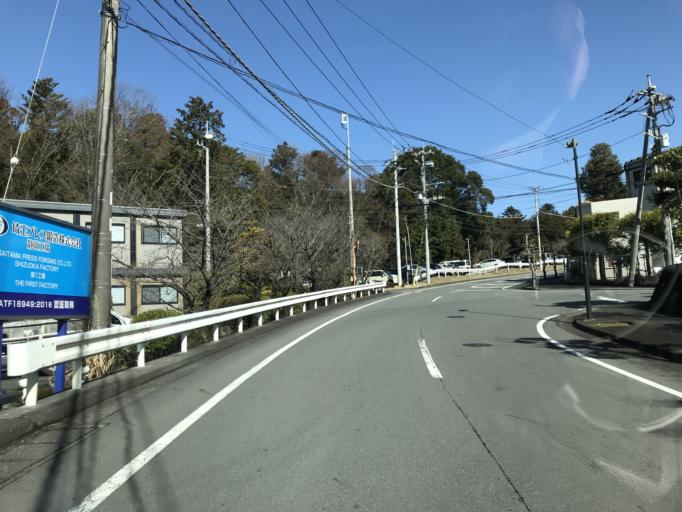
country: JP
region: Shizuoka
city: Fujinomiya
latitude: 35.2678
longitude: 138.6439
